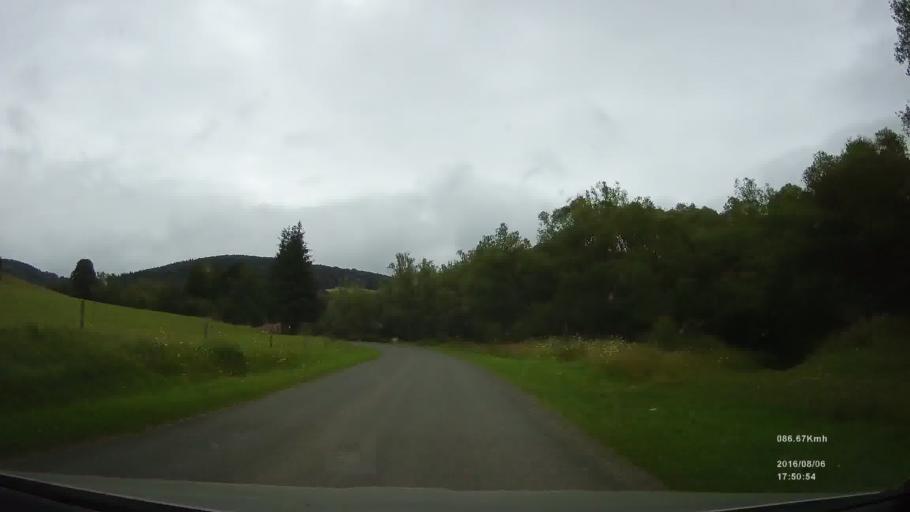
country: SK
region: Presovsky
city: Svidnik
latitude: 49.3965
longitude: 21.5694
